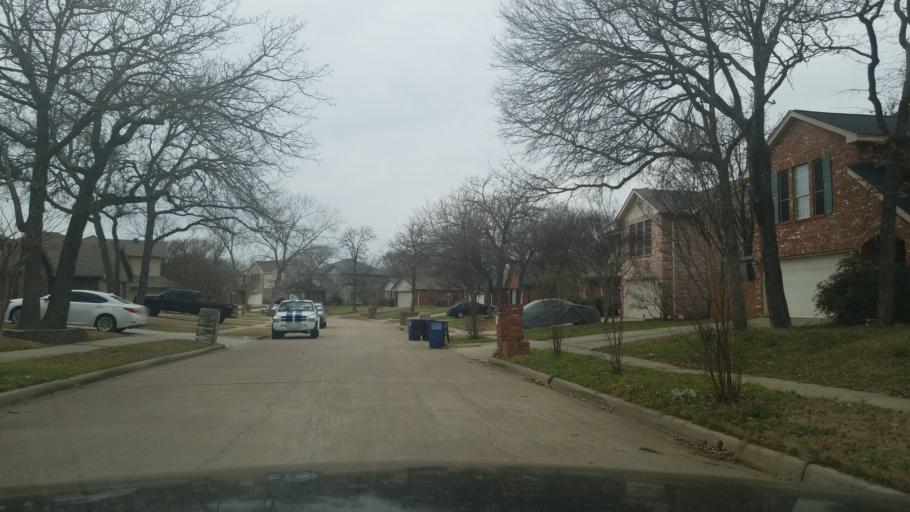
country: US
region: Texas
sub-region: Denton County
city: Corinth
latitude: 33.1372
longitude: -97.0742
